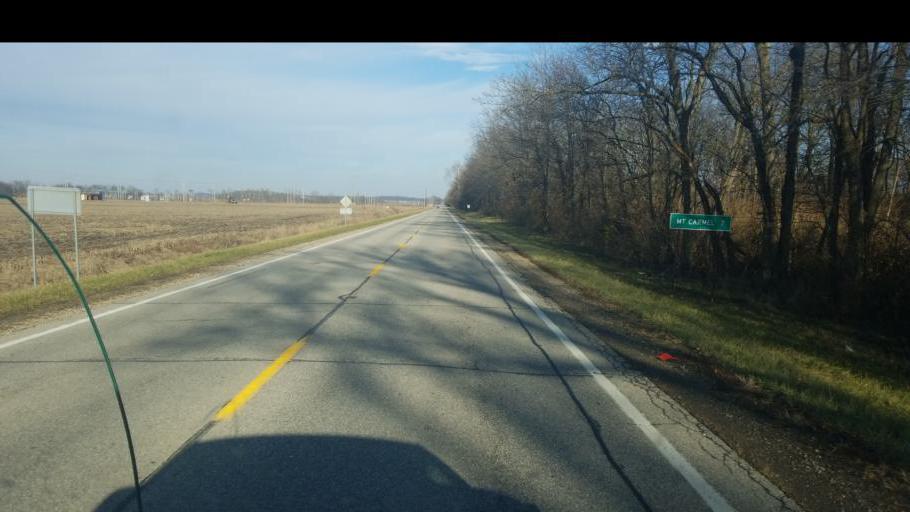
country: US
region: Illinois
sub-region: Wabash County
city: Mount Carmel
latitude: 38.3540
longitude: -87.8657
